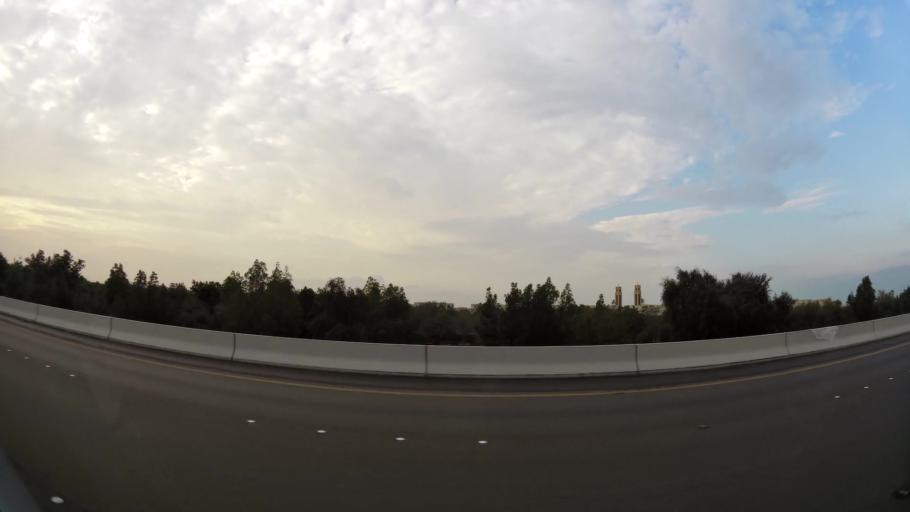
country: AE
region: Abu Dhabi
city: Abu Dhabi
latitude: 24.4020
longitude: 54.4908
